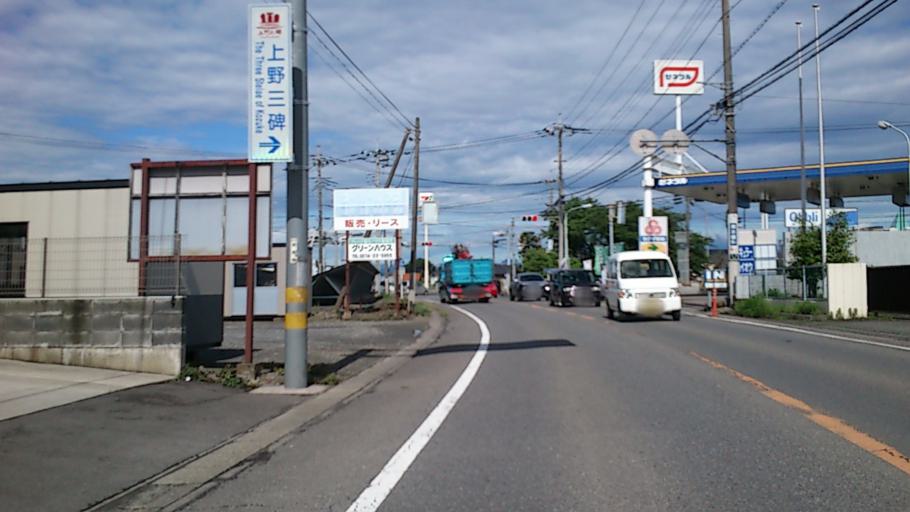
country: JP
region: Gunma
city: Fujioka
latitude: 36.2630
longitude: 139.0590
